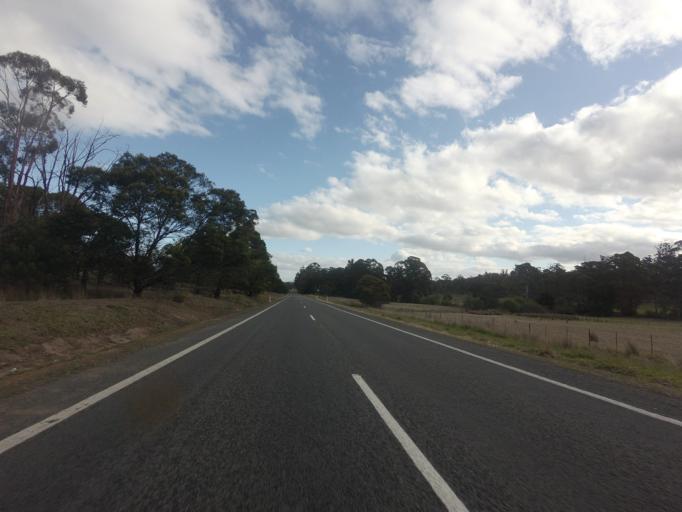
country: AU
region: Tasmania
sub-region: Sorell
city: Sorell
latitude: -42.6939
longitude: 147.5266
